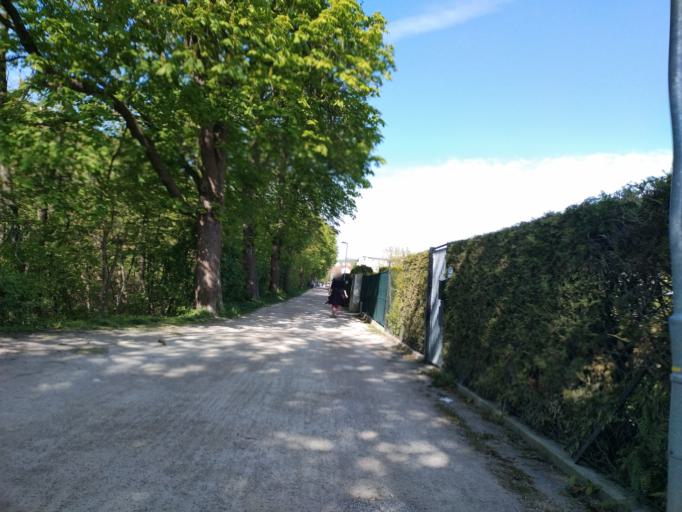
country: AT
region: Lower Austria
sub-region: Politischer Bezirk Wien-Umgebung
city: Purkersdorf
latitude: 48.2063
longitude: 16.1952
